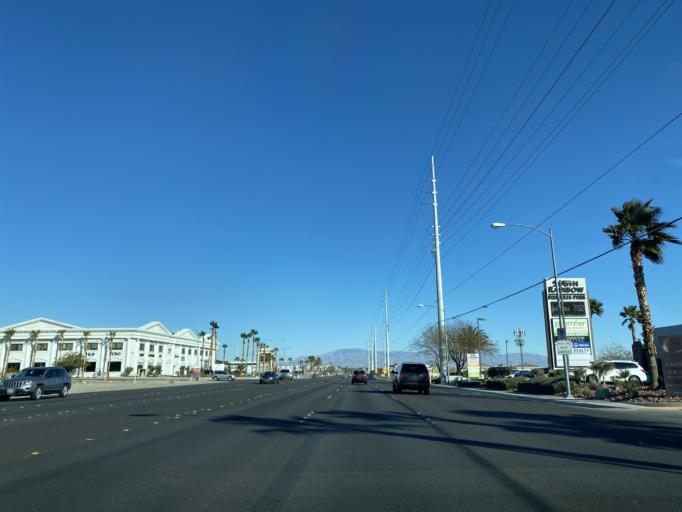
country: US
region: Nevada
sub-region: Clark County
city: Spring Valley
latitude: 36.0806
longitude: -115.2426
